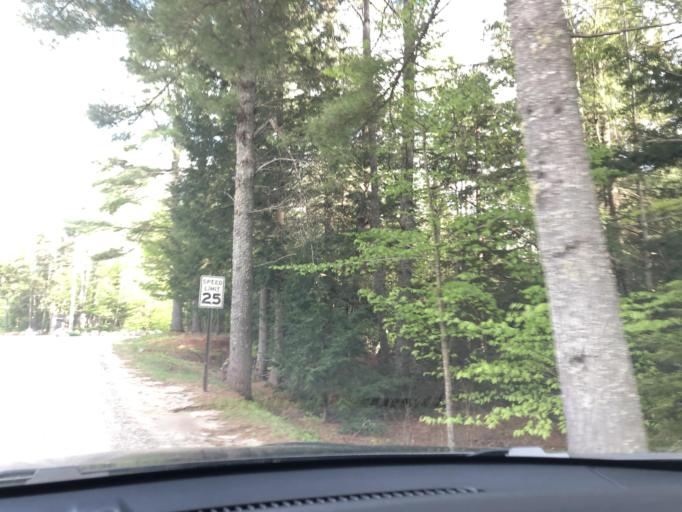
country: US
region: New Hampshire
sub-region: Merrimack County
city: New London
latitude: 43.4043
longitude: -72.0150
